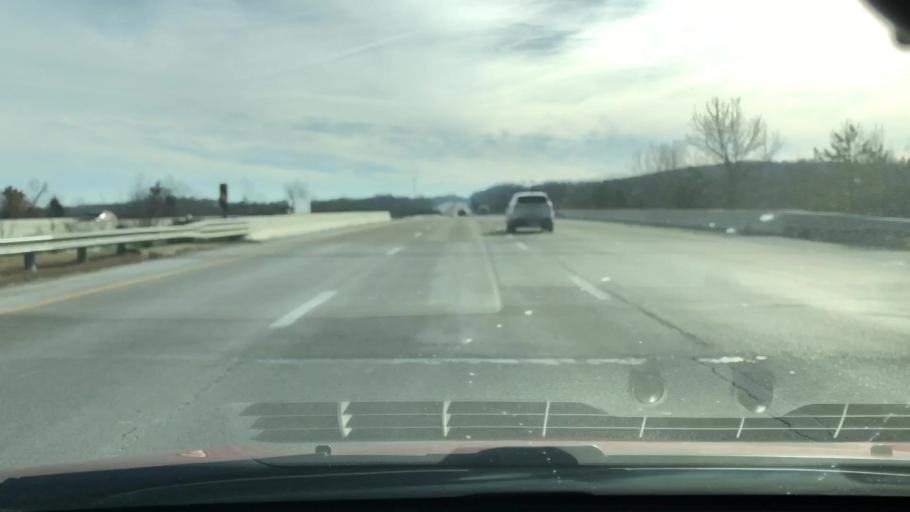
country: US
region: Ohio
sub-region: Greene County
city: Beavercreek
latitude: 39.7284
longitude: -84.0908
